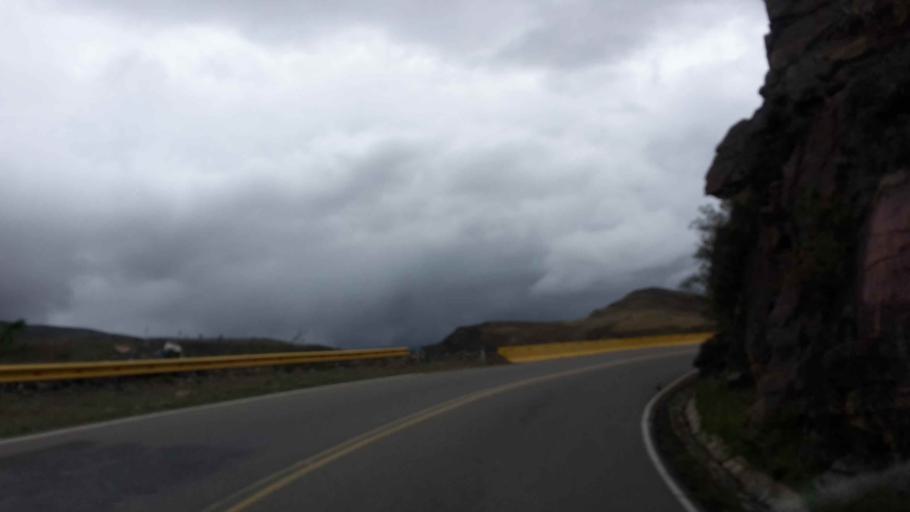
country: BO
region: Cochabamba
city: Punata
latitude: -17.4927
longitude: -65.7929
